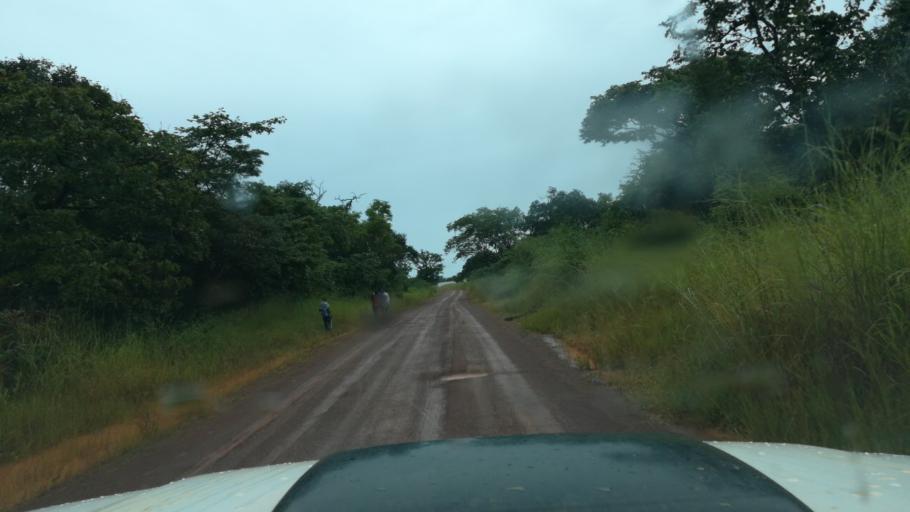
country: ZM
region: Luapula
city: Mwense
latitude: -10.2998
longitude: 28.1191
